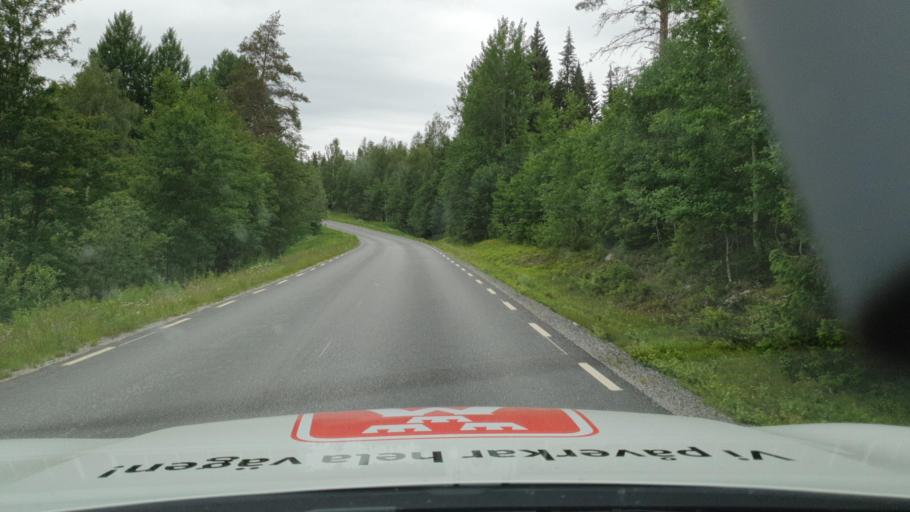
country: SE
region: Vaesterbotten
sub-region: Nordmalings Kommun
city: Nordmaling
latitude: 63.7147
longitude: 19.5728
